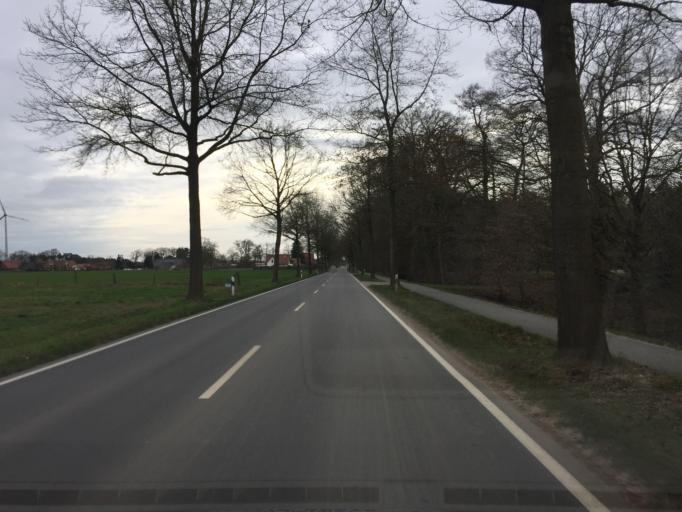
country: DE
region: Lower Saxony
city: Langwedel
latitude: 53.0367
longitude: 9.1619
